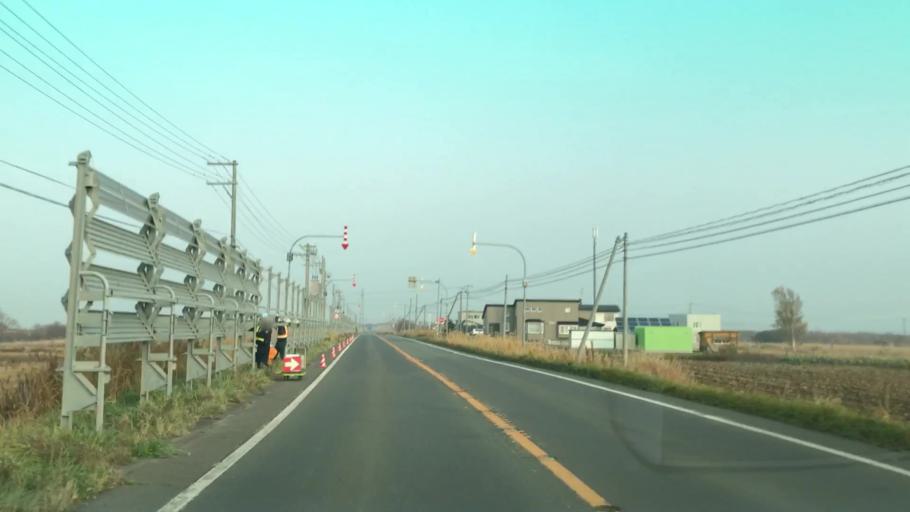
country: JP
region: Hokkaido
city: Ishikari
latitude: 43.2810
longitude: 141.4102
